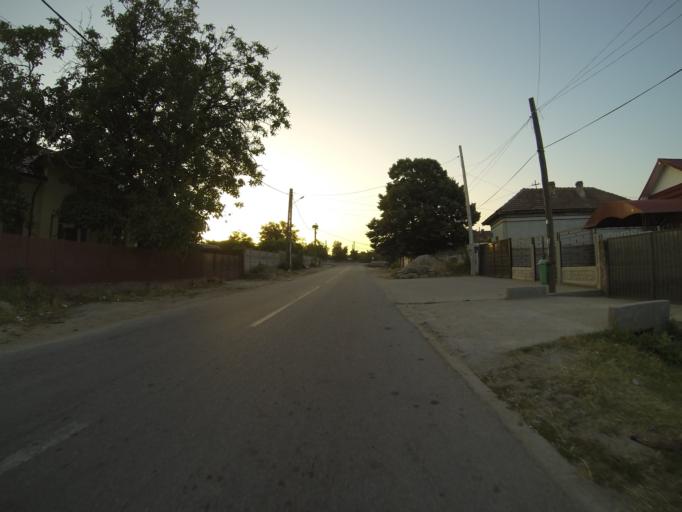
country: RO
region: Dolj
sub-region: Comuna Dobresti
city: Dobresti
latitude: 43.9840
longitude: 23.9406
